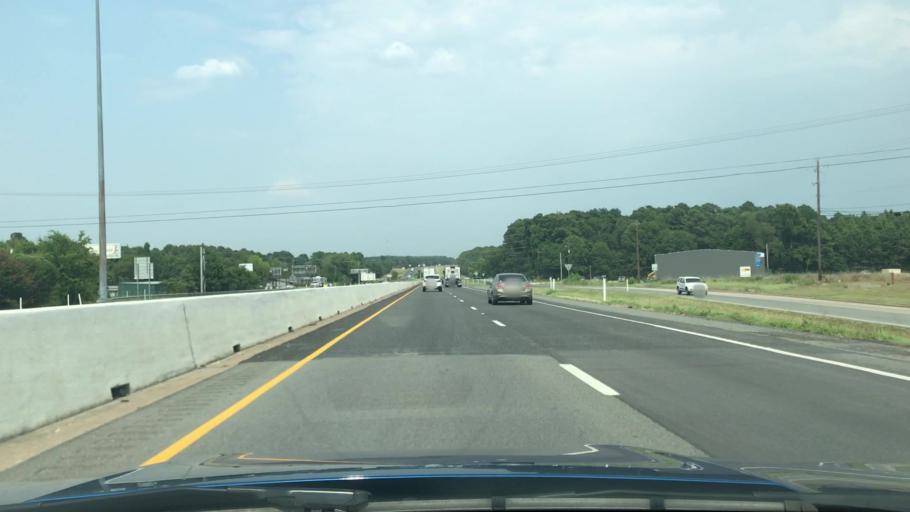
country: US
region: Texas
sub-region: Gregg County
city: Longview
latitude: 32.4507
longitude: -94.7072
